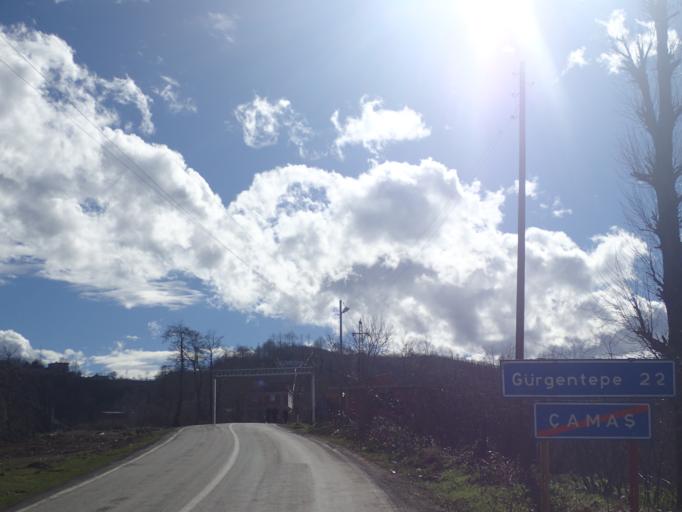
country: TR
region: Ordu
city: Camas
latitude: 40.8950
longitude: 37.5281
